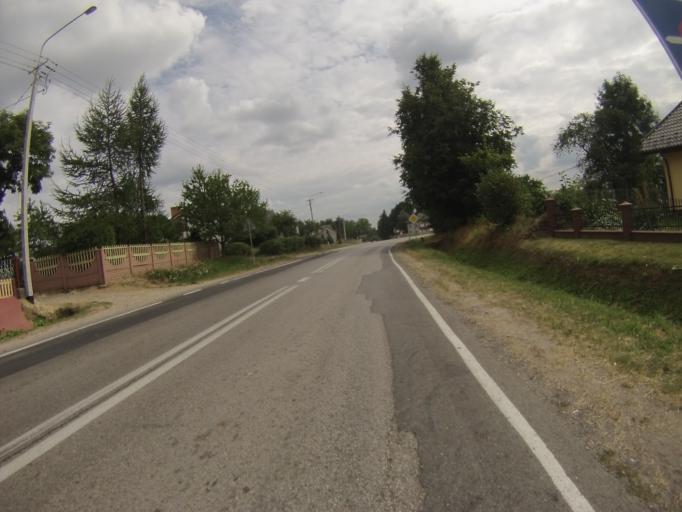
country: PL
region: Swietokrzyskie
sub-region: Powiat kielecki
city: Lagow
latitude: 50.7359
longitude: 21.0757
